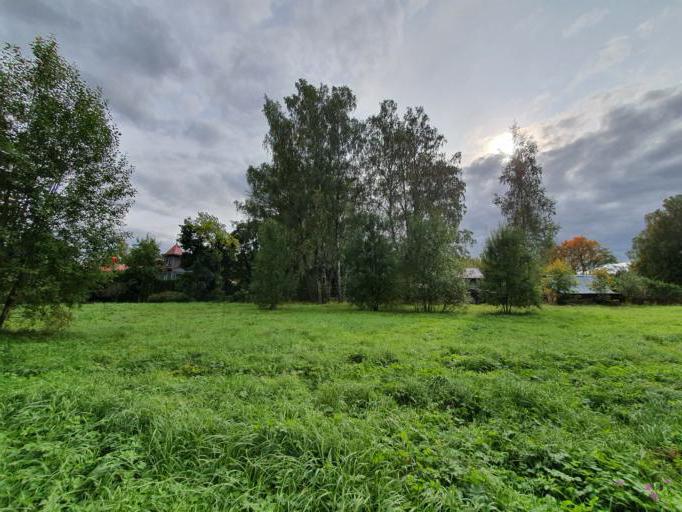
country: RU
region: St.-Petersburg
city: Pavlovsk
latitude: 59.6900
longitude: 30.4378
